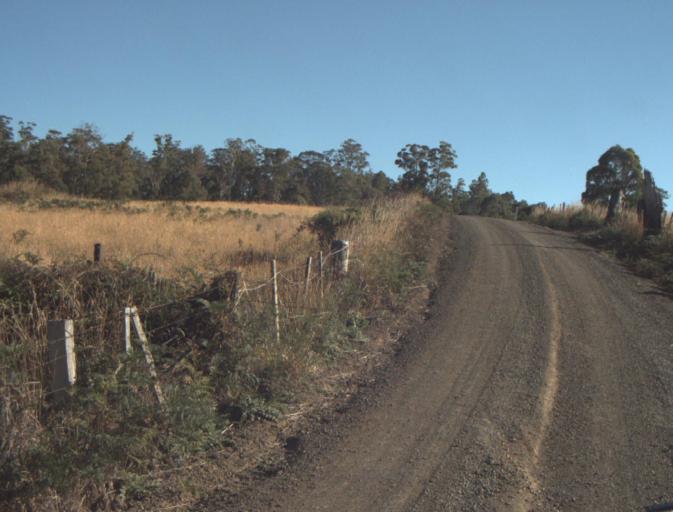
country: AU
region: Tasmania
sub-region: Launceston
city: Newstead
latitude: -41.4110
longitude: 147.2885
